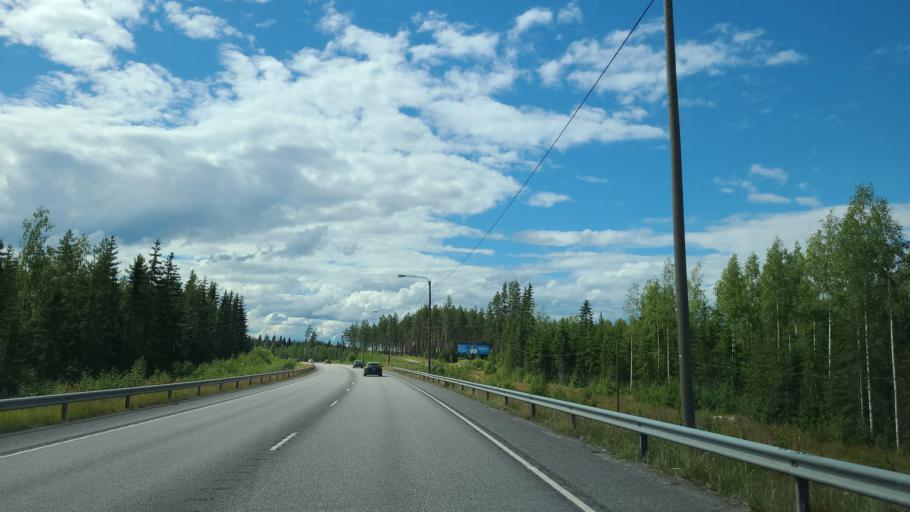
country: FI
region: Central Finland
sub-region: Jyvaeskylae
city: Toivakka
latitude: 62.2488
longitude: 26.0205
